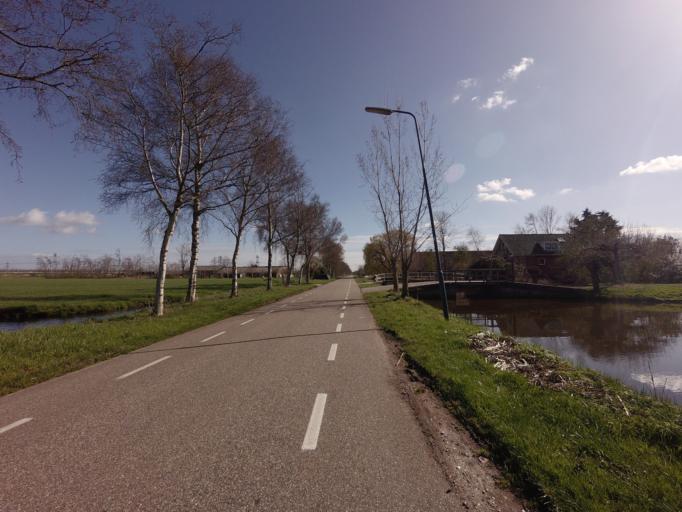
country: NL
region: Utrecht
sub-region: Stichtse Vecht
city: Breukelen
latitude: 52.1631
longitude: 4.9775
